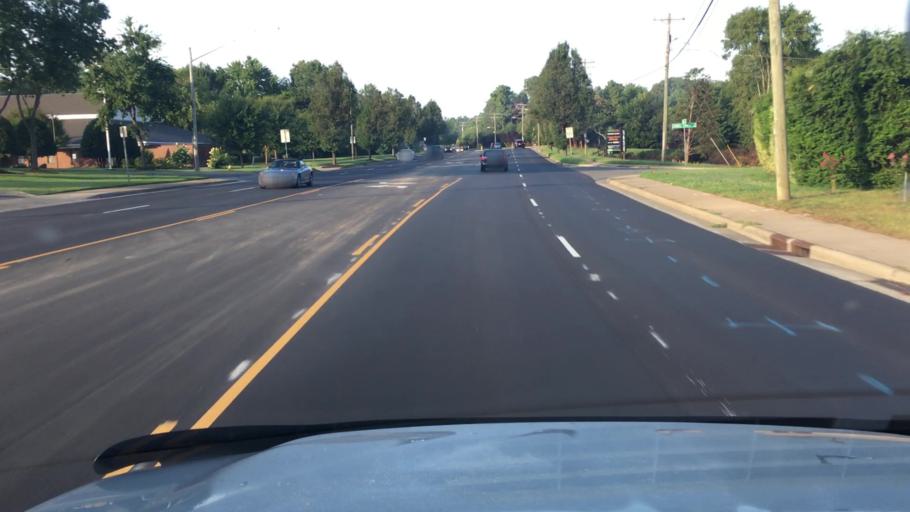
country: US
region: North Carolina
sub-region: Mecklenburg County
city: Pineville
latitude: 35.0990
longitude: -80.8381
